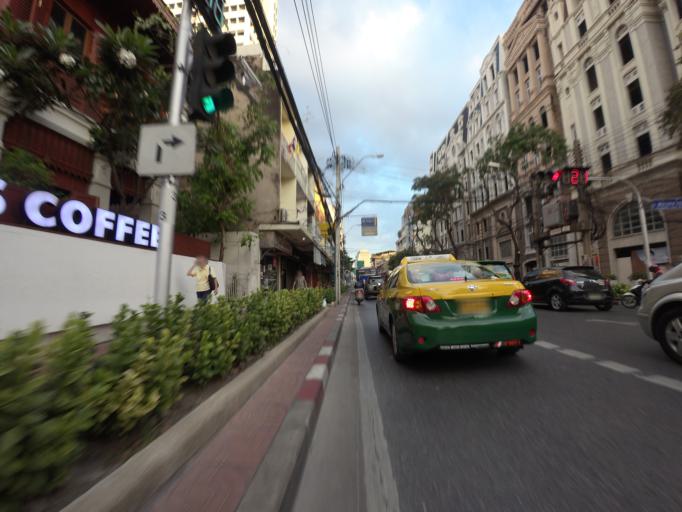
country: TH
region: Bangkok
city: Pom Prap Sattru Phai
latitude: 13.7500
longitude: 100.5145
